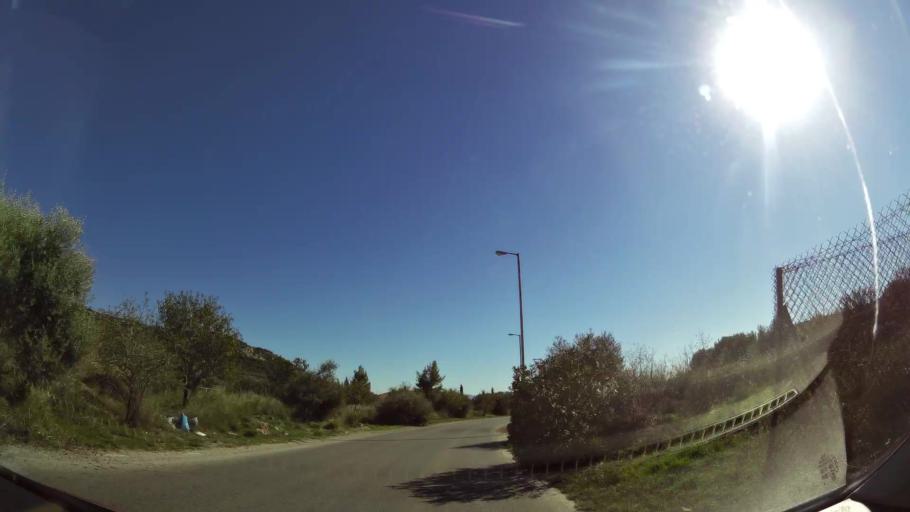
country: GR
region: Attica
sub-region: Nomarchia Anatolikis Attikis
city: Paiania
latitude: 37.9661
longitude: 23.8639
